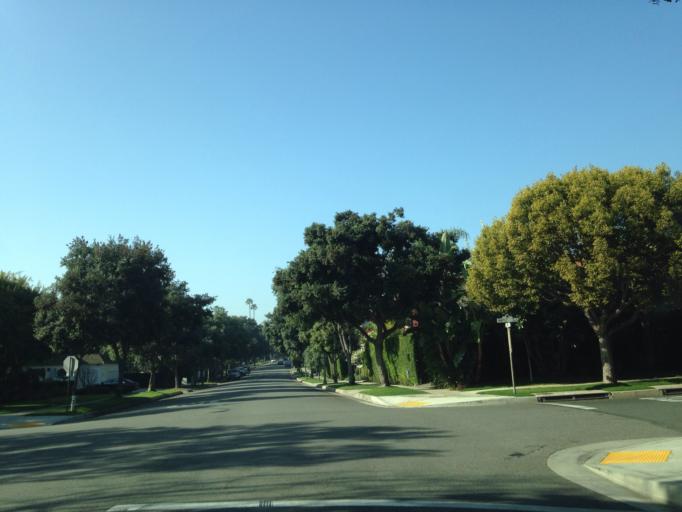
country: US
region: California
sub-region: Los Angeles County
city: Beverly Hills
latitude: 34.0833
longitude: -118.4001
